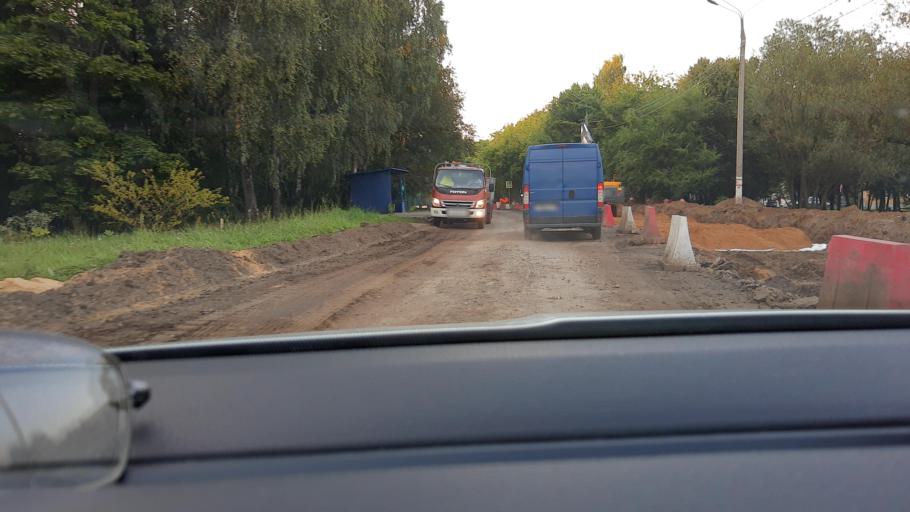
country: RU
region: Moskovskaya
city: Troitsk
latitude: 55.3130
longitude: 37.1749
